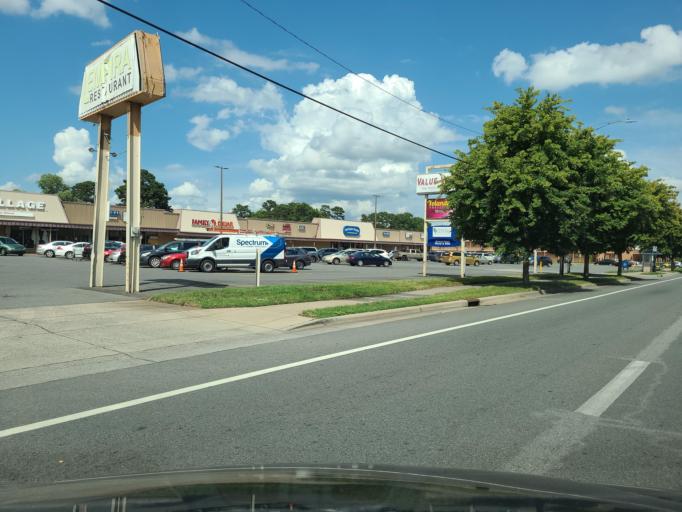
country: US
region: North Carolina
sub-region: Mecklenburg County
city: Charlotte
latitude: 35.2136
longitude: -80.7691
